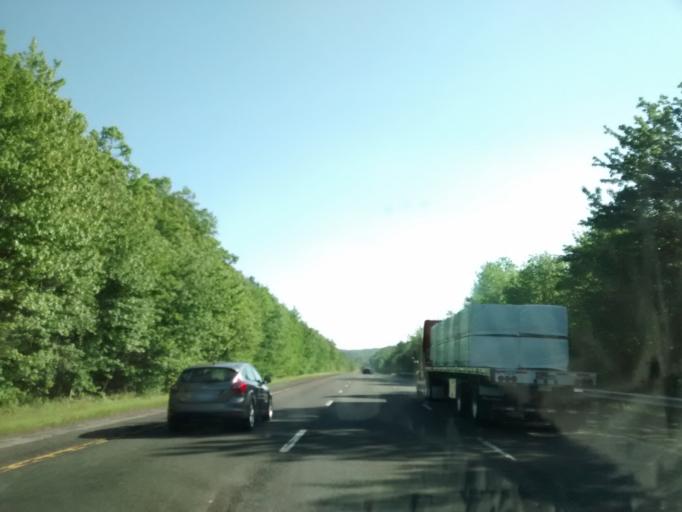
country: US
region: Massachusetts
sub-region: Hampden County
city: Holland
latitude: 42.0394
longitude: -72.1288
